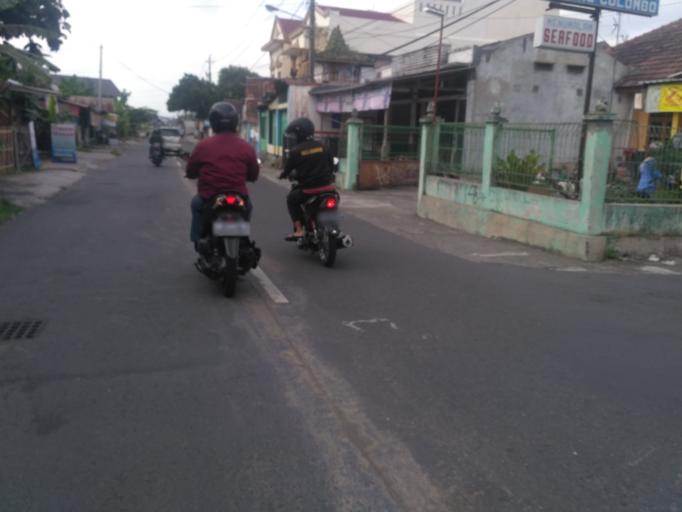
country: ID
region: Daerah Istimewa Yogyakarta
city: Yogyakarta
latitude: -7.7696
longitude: 110.3568
